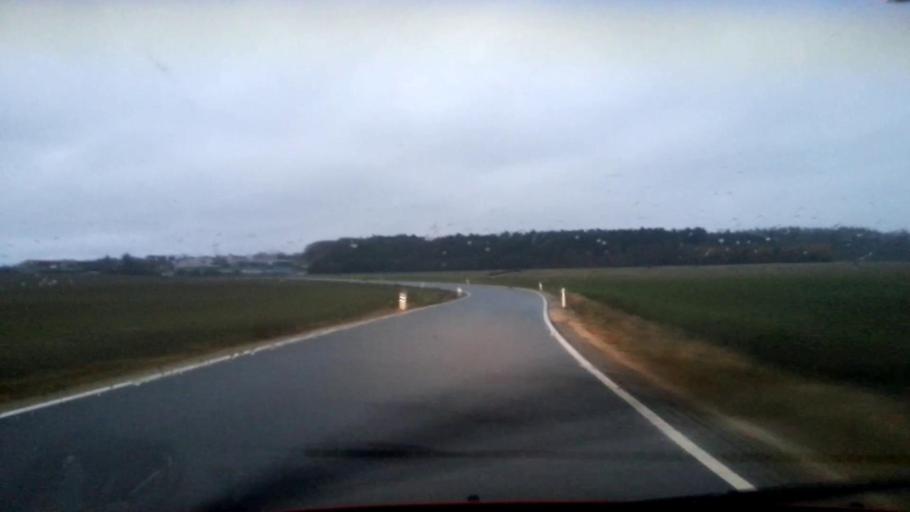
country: DE
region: Bavaria
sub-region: Upper Franconia
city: Poxdorf
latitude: 49.9643
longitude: 11.1368
